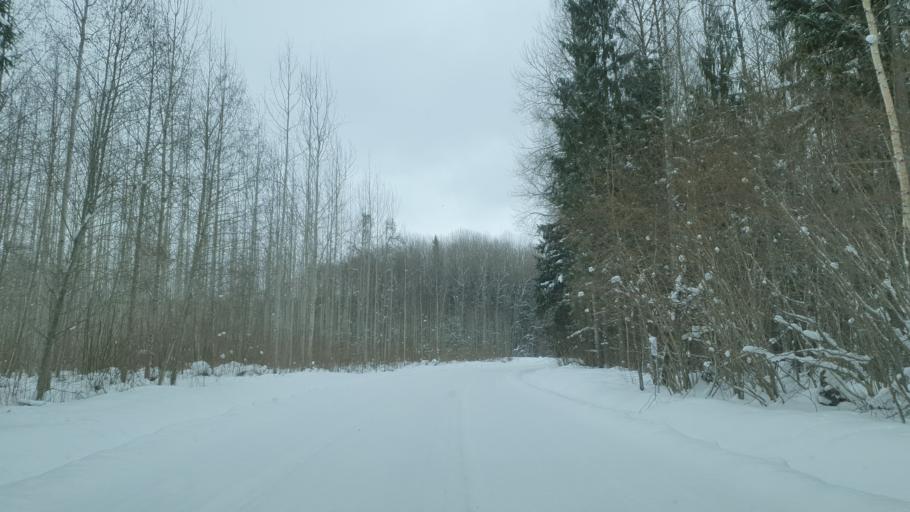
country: EE
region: Polvamaa
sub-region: Raepina vald
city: Rapina
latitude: 58.1927
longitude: 27.3424
